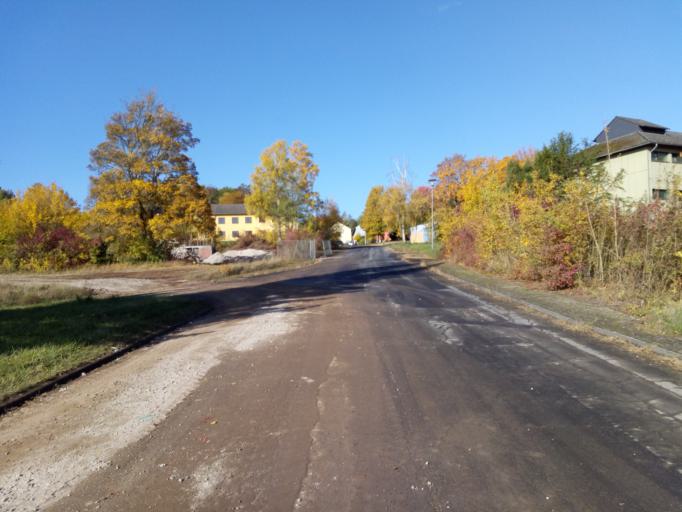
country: DE
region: Rheinland-Pfalz
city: Nussbaum
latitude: 49.8079
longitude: 7.6377
